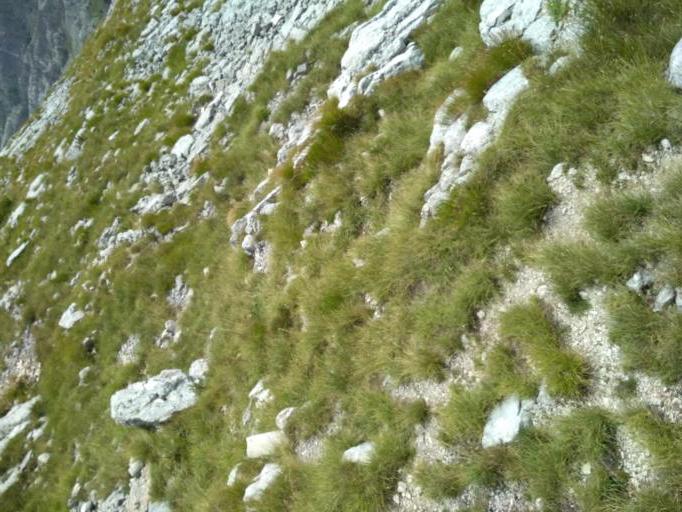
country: ME
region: Kotor
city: Kotor
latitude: 42.3997
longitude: 18.8376
